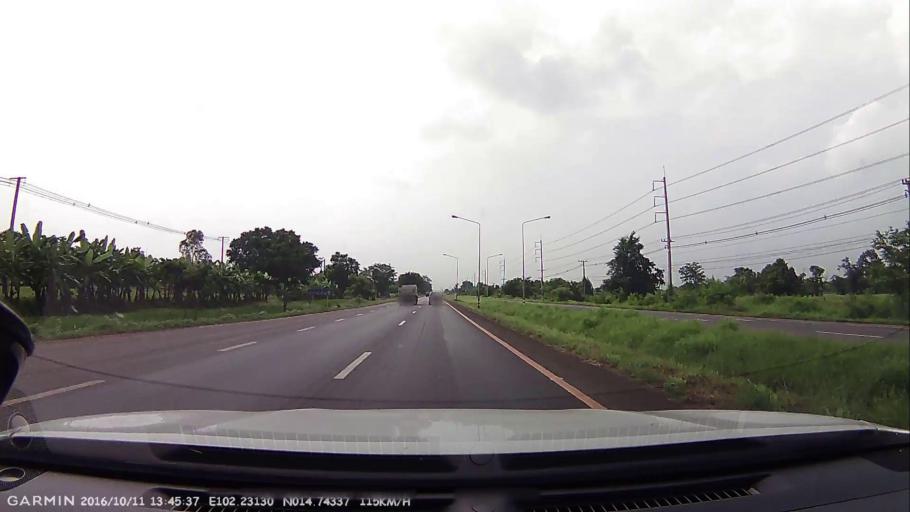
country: TH
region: Nakhon Ratchasima
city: Chok Chai
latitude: 14.7433
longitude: 102.2314
